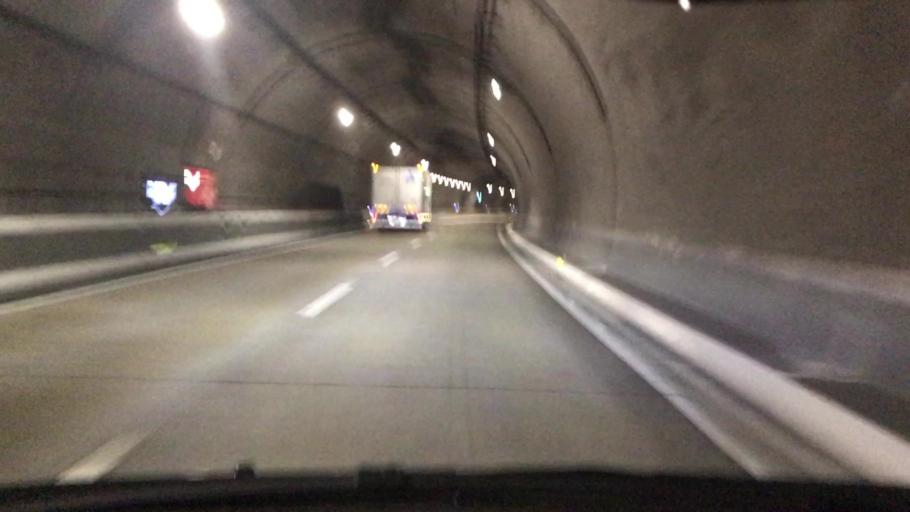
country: JP
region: Hyogo
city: Sandacho
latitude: 34.8066
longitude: 135.2466
